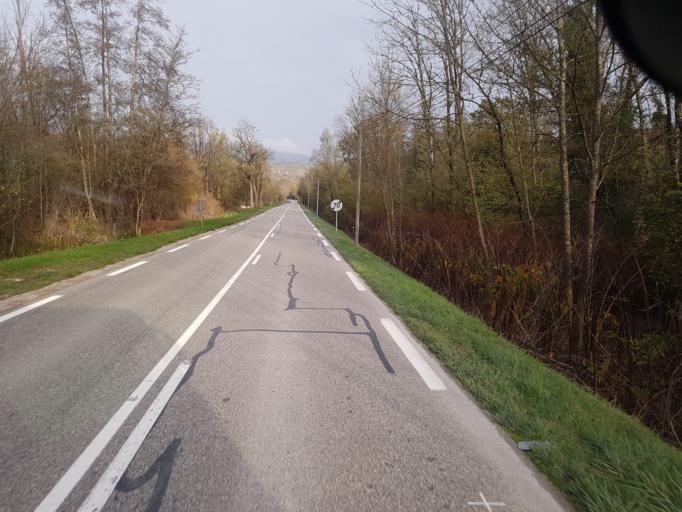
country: FR
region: Rhone-Alpes
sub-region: Departement de la Haute-Savoie
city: Frangy
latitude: 46.0219
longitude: 5.8763
